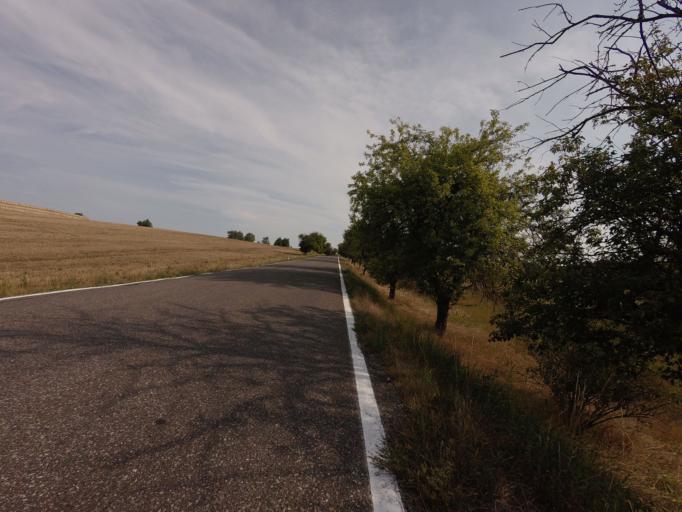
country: CZ
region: Jihocesky
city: Milevsko
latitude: 49.4782
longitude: 14.3659
